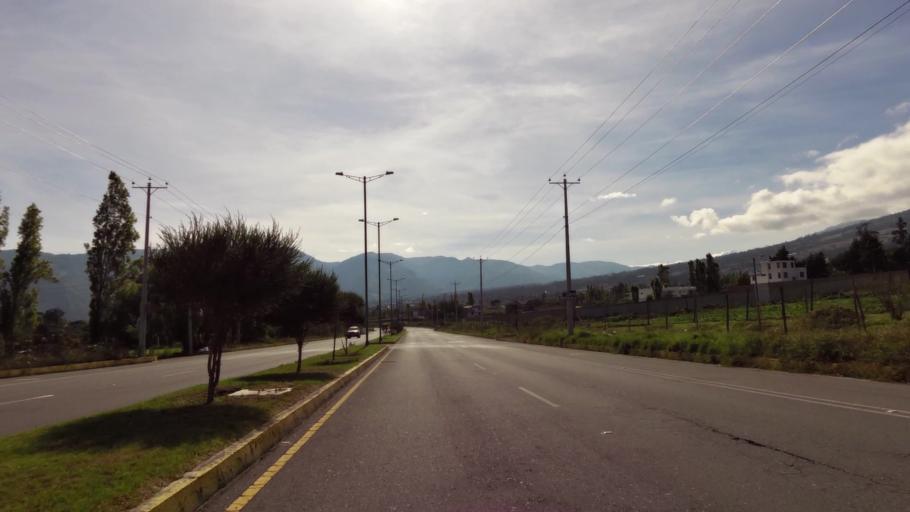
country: EC
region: Imbabura
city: Ibarra
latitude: 0.3321
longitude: -78.1541
